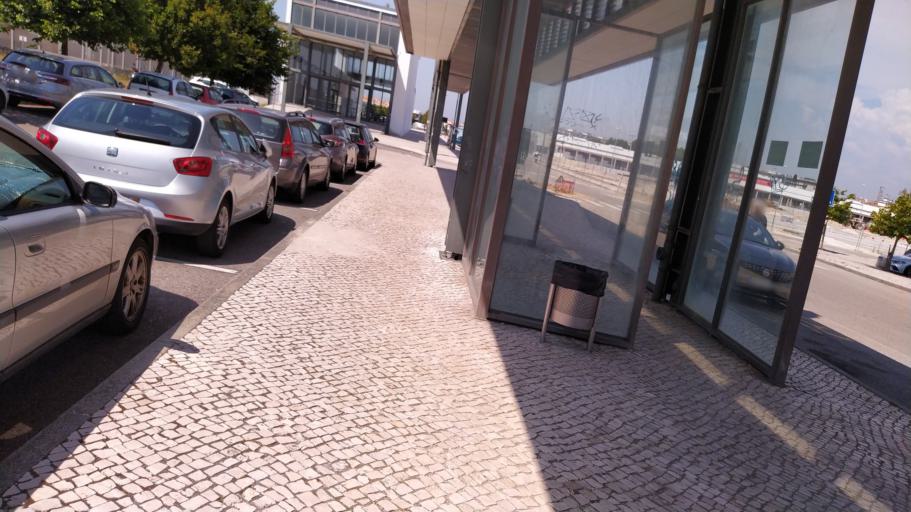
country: PT
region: Aveiro
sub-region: Aveiro
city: Aveiro
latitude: 40.6422
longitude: -8.6403
